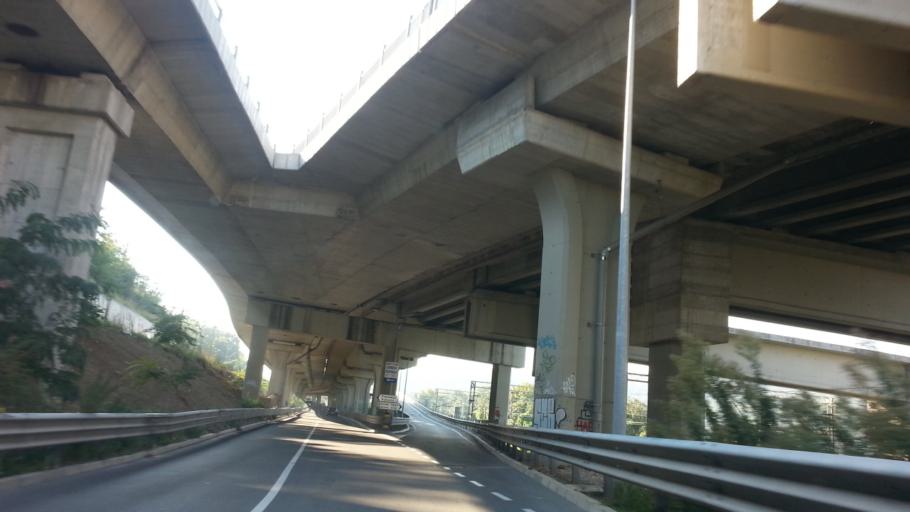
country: RS
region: Central Serbia
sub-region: Belgrade
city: Cukarica
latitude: 44.7891
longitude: 20.4298
